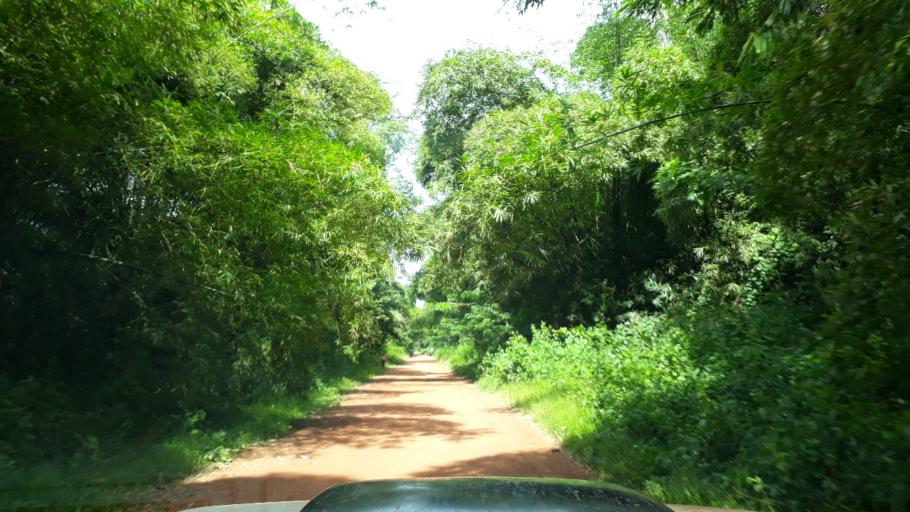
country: CD
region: Eastern Province
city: Buta
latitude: 2.8786
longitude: 24.4669
